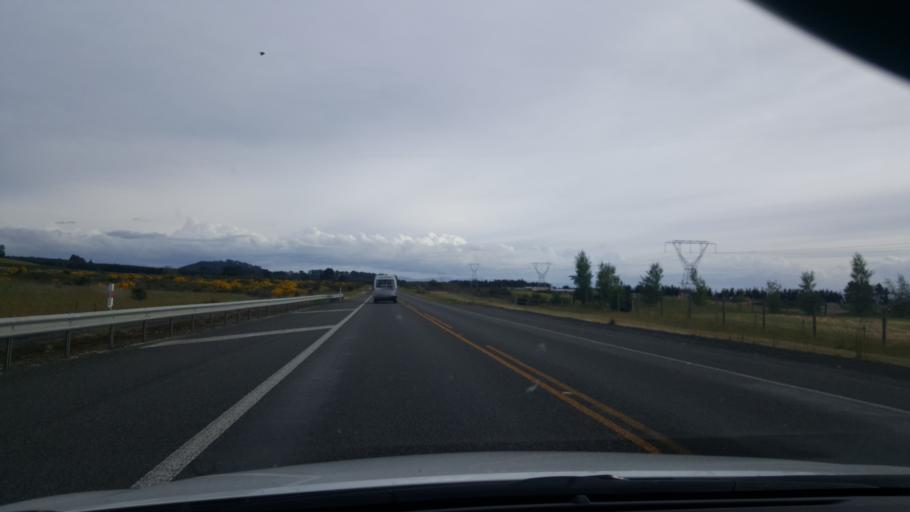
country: NZ
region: Waikato
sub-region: Taupo District
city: Taupo
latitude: -38.6875
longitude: 176.1140
